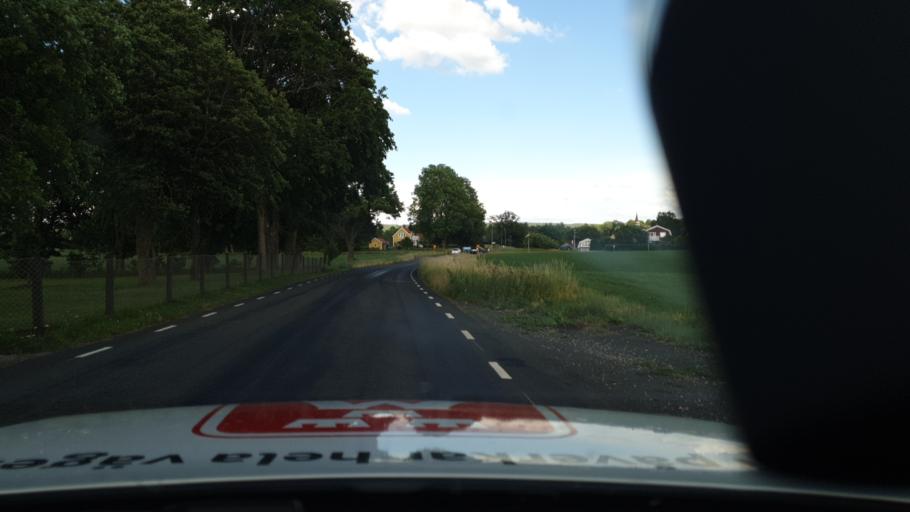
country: SE
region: Vaestra Goetaland
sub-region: Skara Kommun
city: Axvall
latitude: 58.3867
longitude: 13.6353
